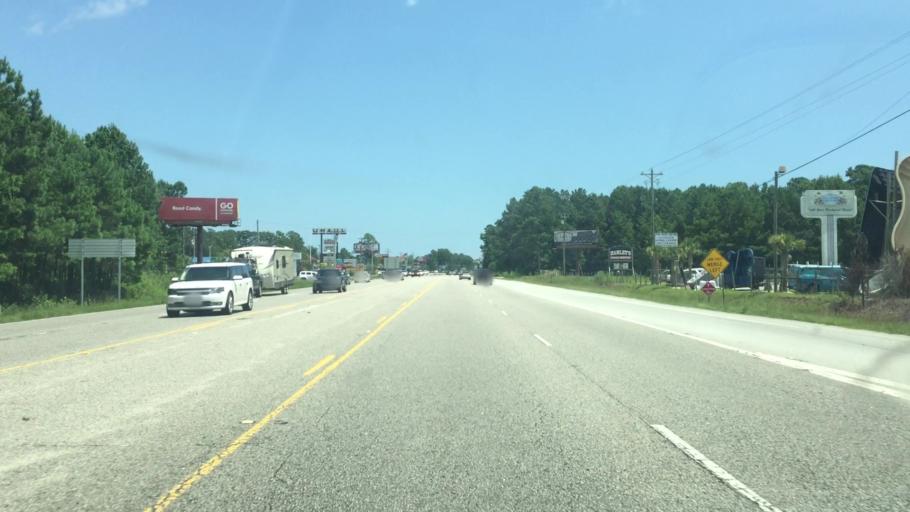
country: US
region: South Carolina
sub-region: Horry County
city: North Myrtle Beach
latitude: 33.8749
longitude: -78.6804
